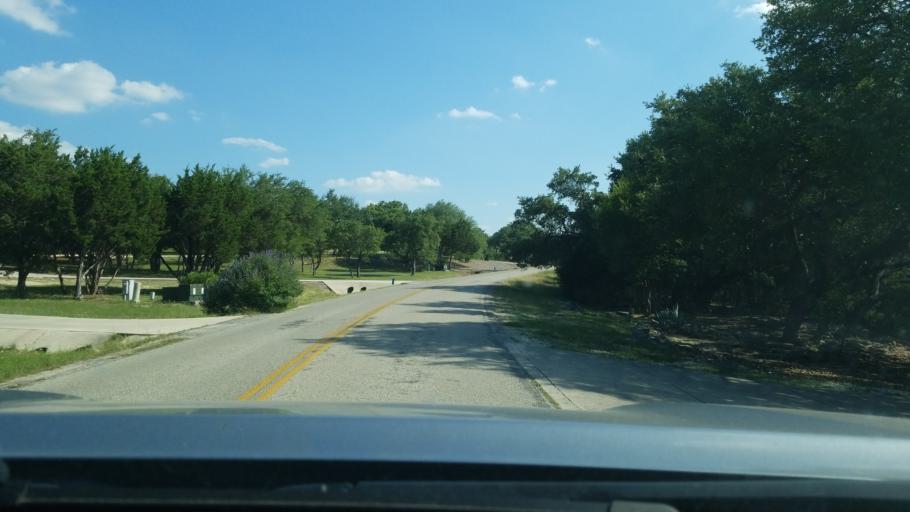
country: US
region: Texas
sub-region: Comal County
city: Bulverde
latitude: 29.8179
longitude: -98.4000
